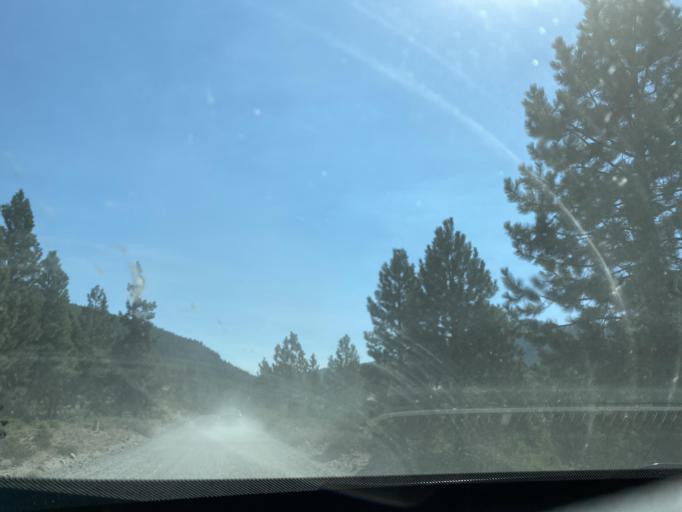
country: US
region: Oregon
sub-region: Deschutes County
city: Sunriver
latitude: 44.0345
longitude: -121.5329
